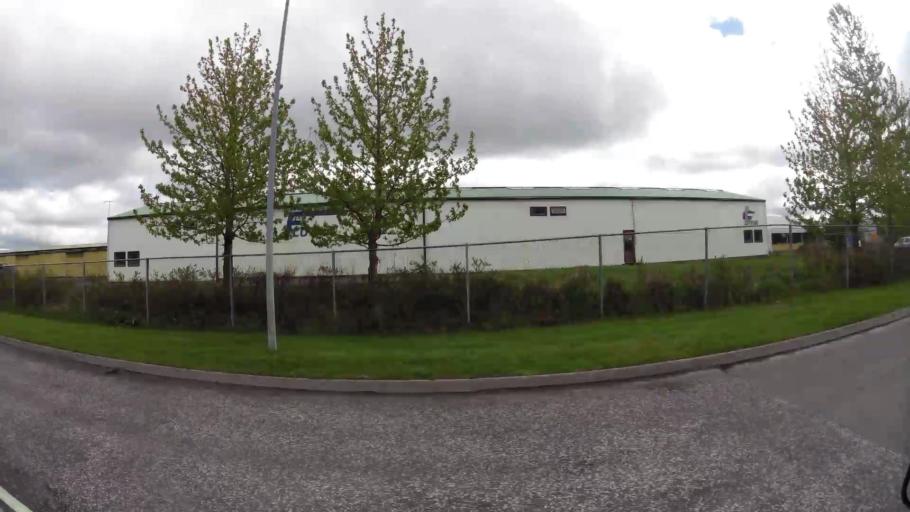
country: IS
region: Capital Region
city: Kopavogur
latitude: 64.1347
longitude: -21.9458
